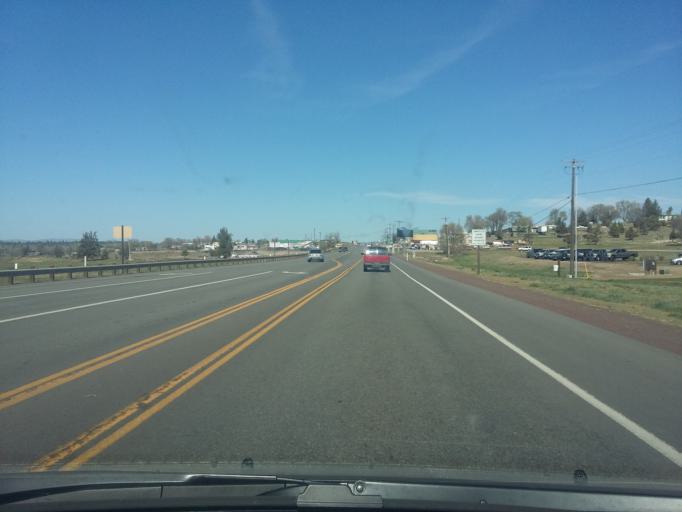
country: US
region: Oregon
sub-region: Jefferson County
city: Madras
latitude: 44.6075
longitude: -121.1389
